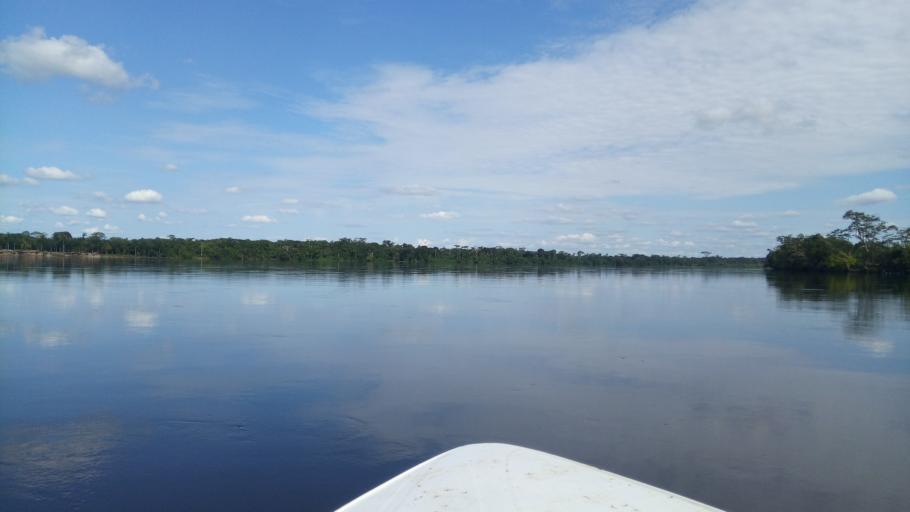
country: CD
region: Eastern Province
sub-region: Sous-Region de la Tshopo
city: Yangambi
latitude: 0.5511
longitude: 24.2443
